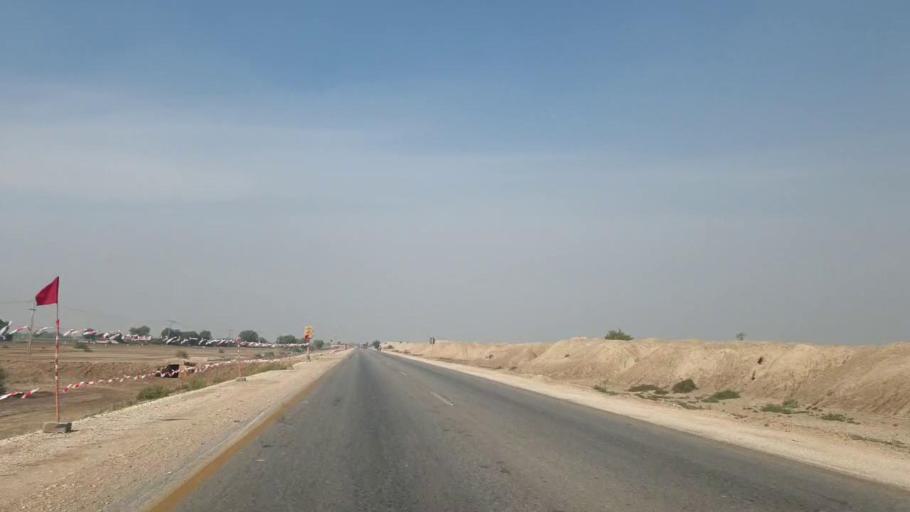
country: PK
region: Sindh
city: Sann
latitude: 25.9693
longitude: 68.1889
